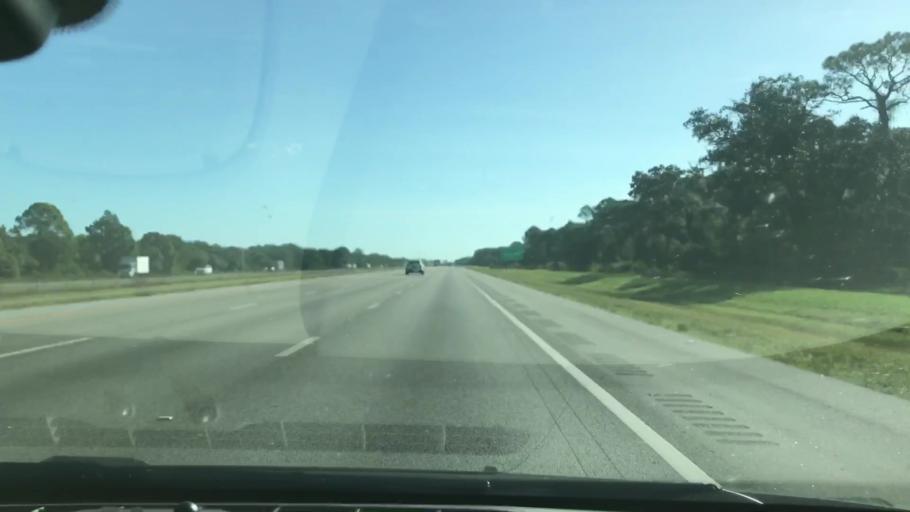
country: US
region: Florida
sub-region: Sarasota County
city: Warm Mineral Springs
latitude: 27.0990
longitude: -82.2259
